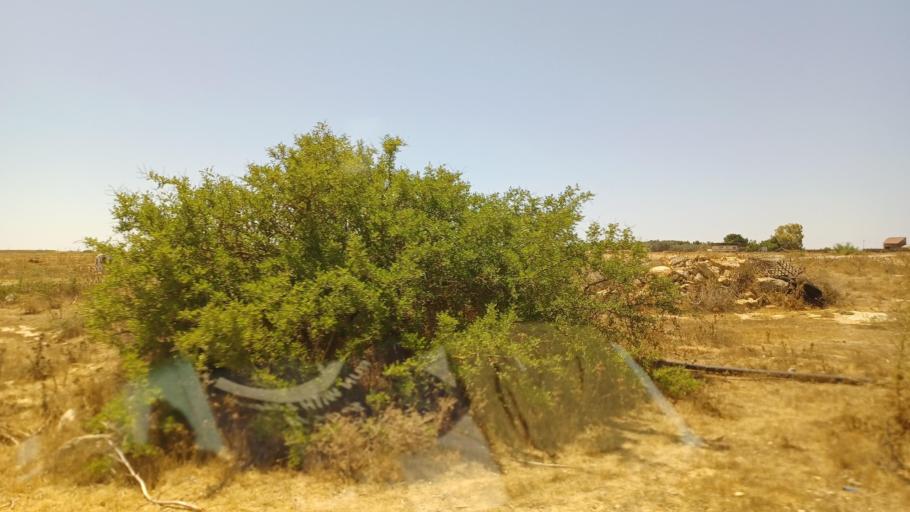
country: CY
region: Ammochostos
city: Avgorou
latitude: 35.0603
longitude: 33.8504
